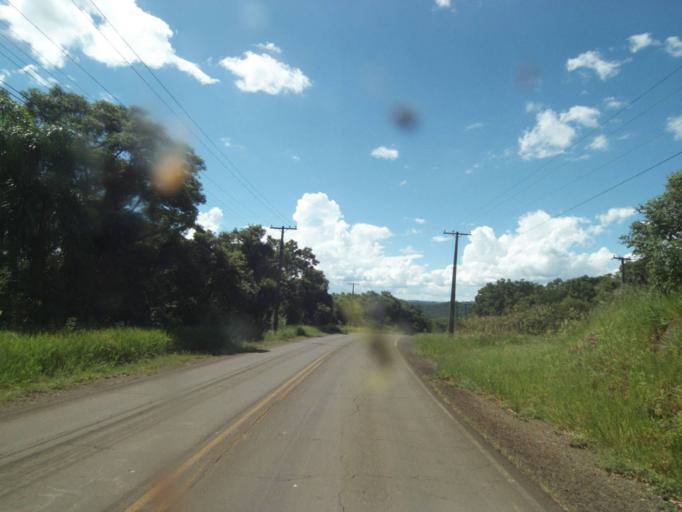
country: BR
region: Parana
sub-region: Chopinzinho
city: Chopinzinho
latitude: -25.7841
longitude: -52.1011
